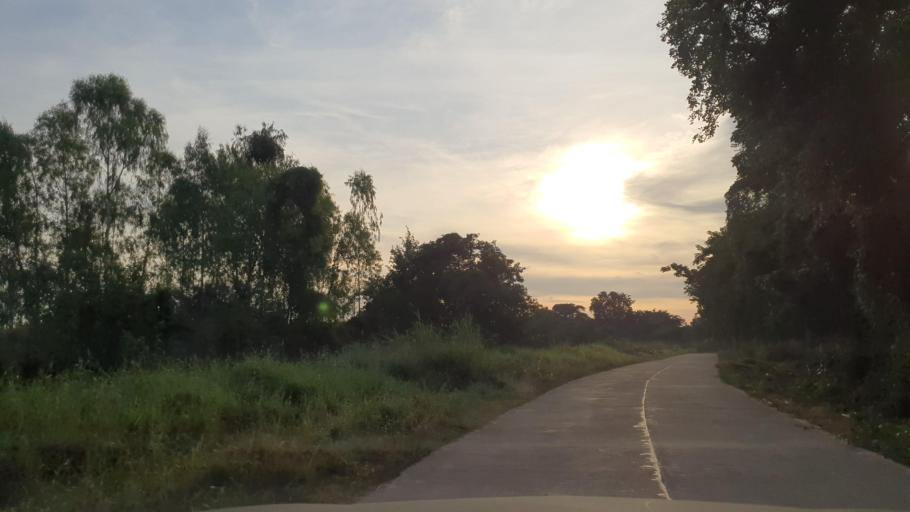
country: TH
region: Nakhon Sawan
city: Krok Phra
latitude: 15.6620
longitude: 100.0172
